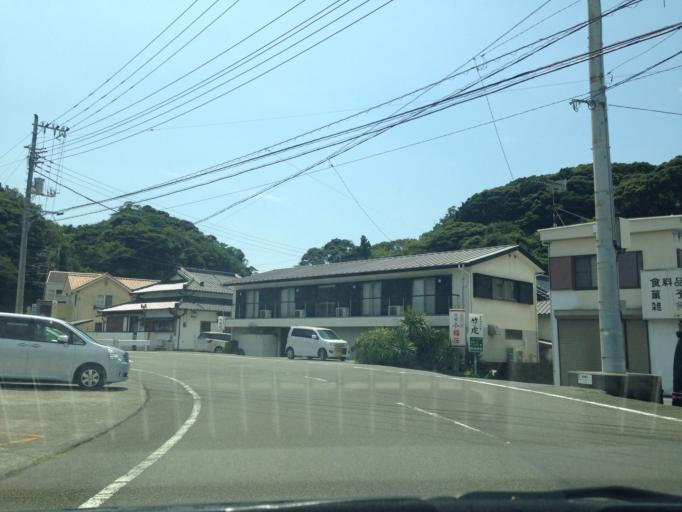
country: JP
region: Shizuoka
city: Shimoda
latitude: 34.6268
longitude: 138.8852
